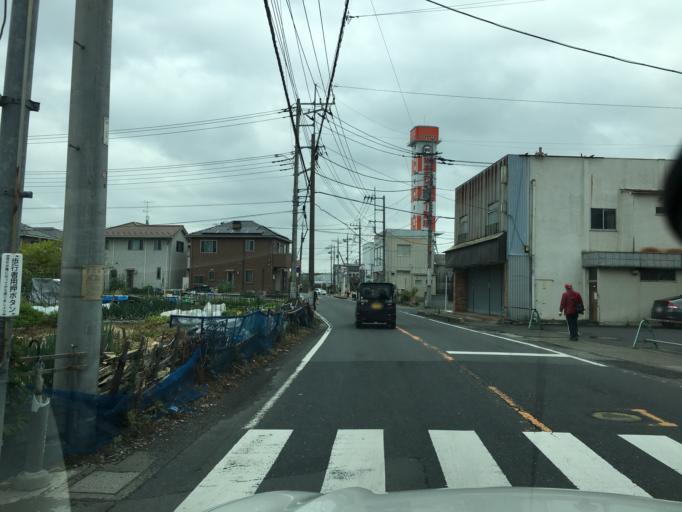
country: JP
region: Saitama
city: Koshigaya
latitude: 35.8632
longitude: 139.7837
